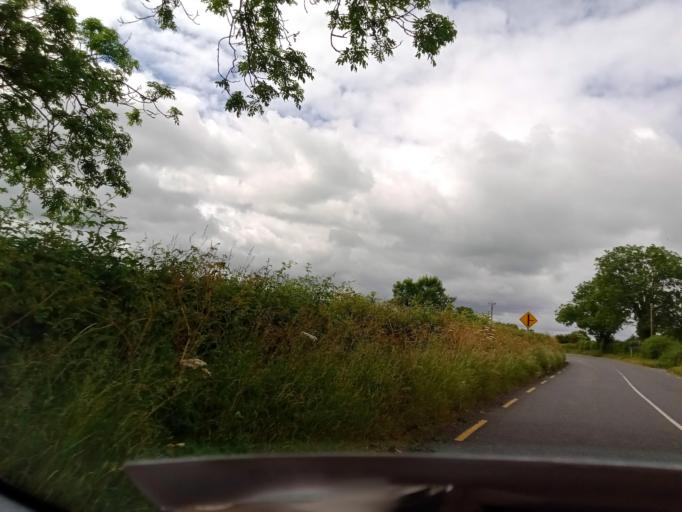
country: IE
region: Leinster
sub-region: Kilkenny
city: Thomastown
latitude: 52.4827
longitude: -7.2499
